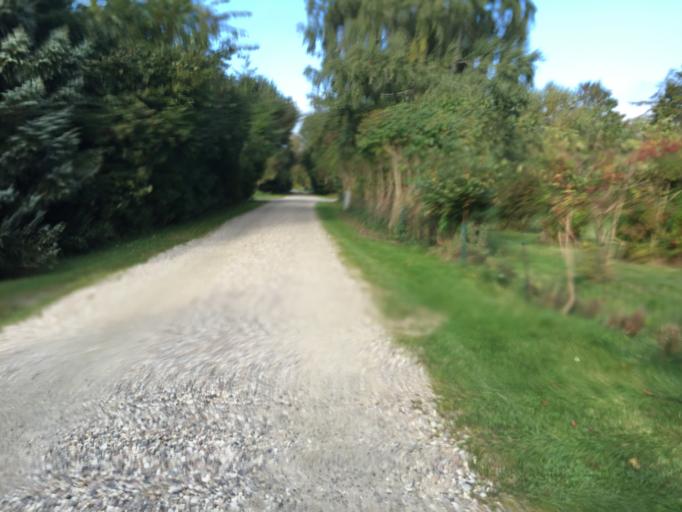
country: DK
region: Zealand
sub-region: Odsherred Kommune
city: Hojby
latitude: 55.8987
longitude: 11.5612
